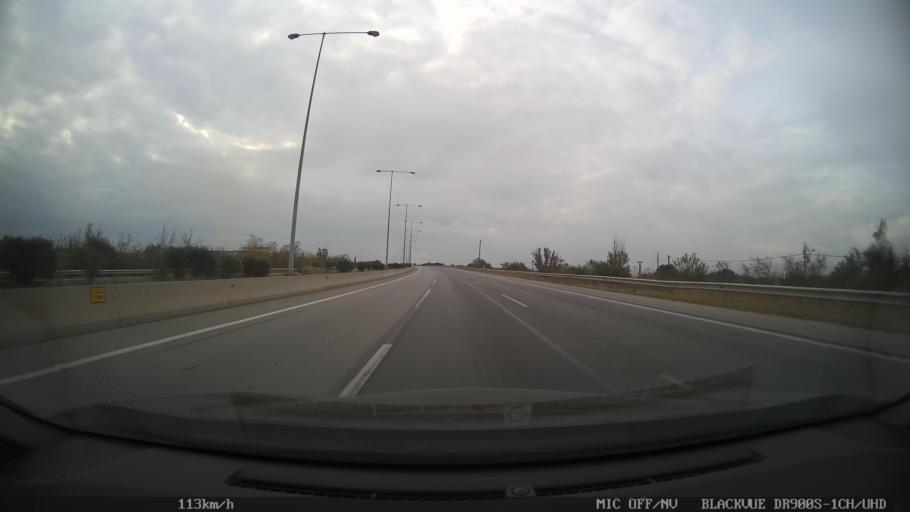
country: GR
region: Central Macedonia
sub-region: Nomos Thessalonikis
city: Nea Magnisia
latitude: 40.6729
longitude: 22.8328
